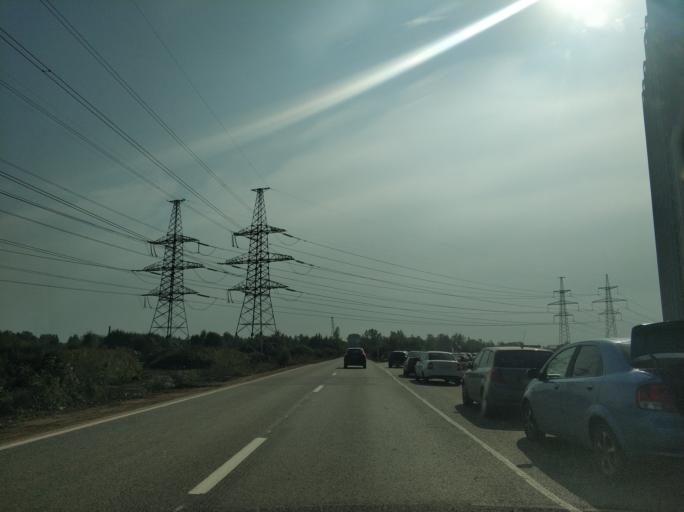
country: RU
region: St.-Petersburg
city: Krasnogvargeisky
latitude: 60.0098
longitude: 30.4831
